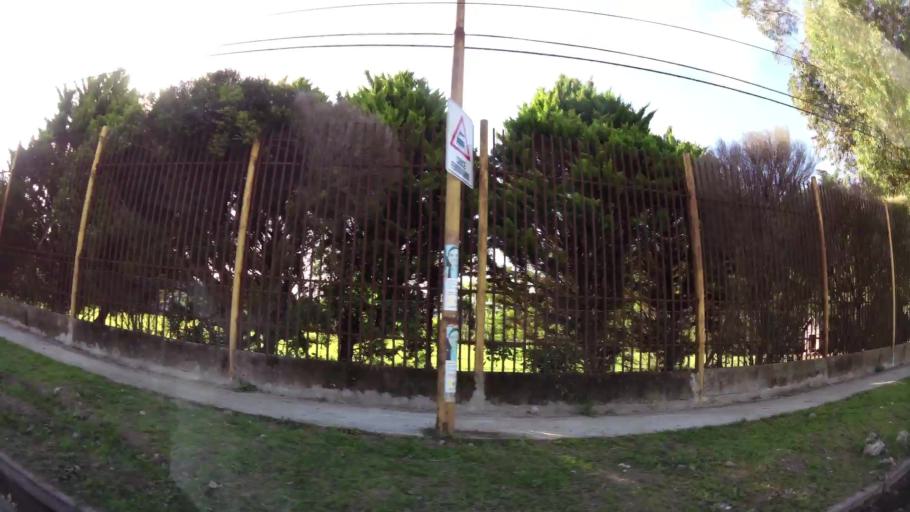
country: AR
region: Buenos Aires
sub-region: Partido de Quilmes
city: Quilmes
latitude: -34.8220
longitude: -58.2212
